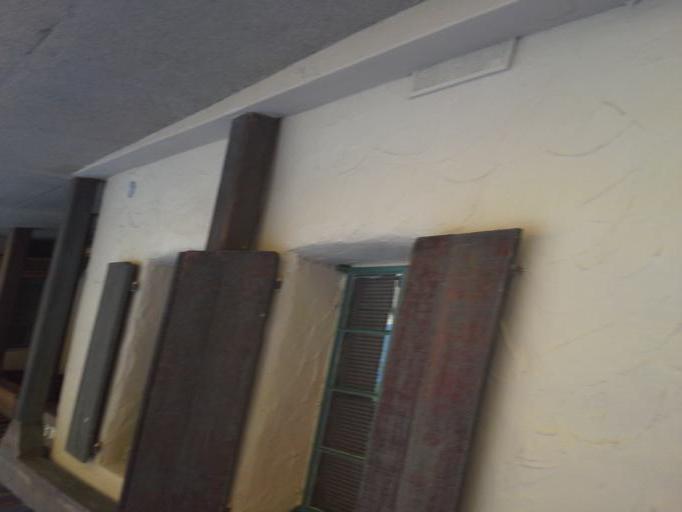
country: US
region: Arizona
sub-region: Pinal County
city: Coolidge
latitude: 32.9949
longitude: -111.5367
